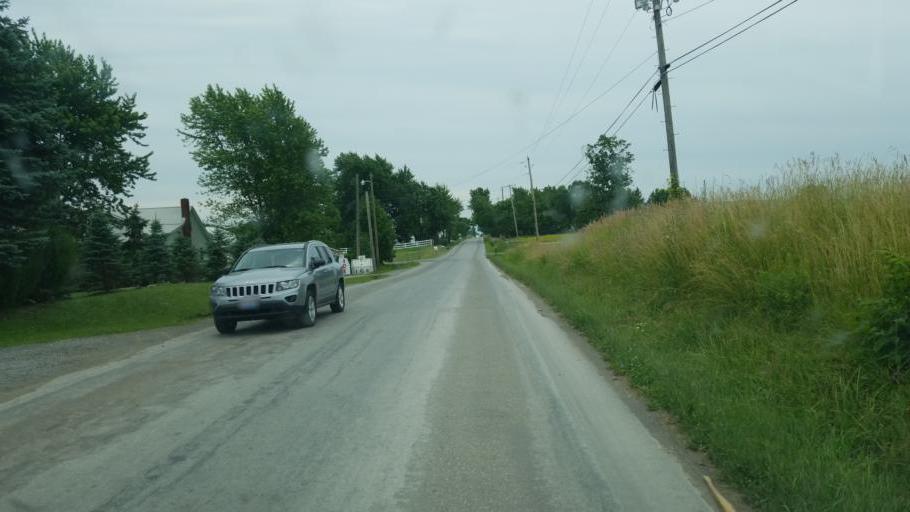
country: US
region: Ohio
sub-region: Geauga County
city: Middlefield
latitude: 41.4769
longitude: -81.0033
